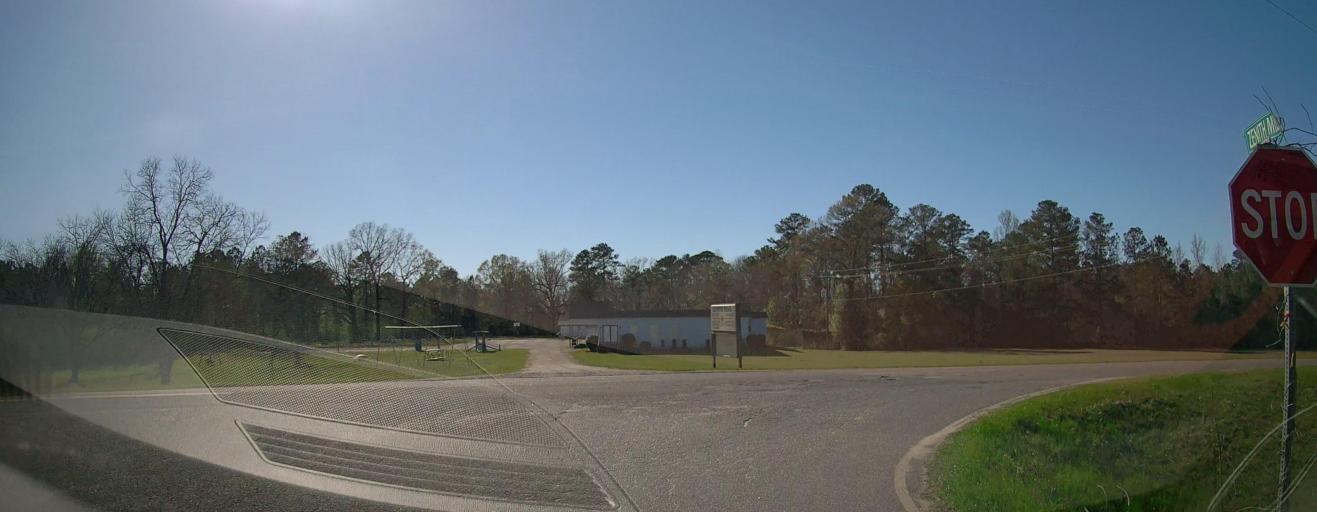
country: US
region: Georgia
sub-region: Peach County
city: Fort Valley
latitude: 32.6122
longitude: -83.9832
